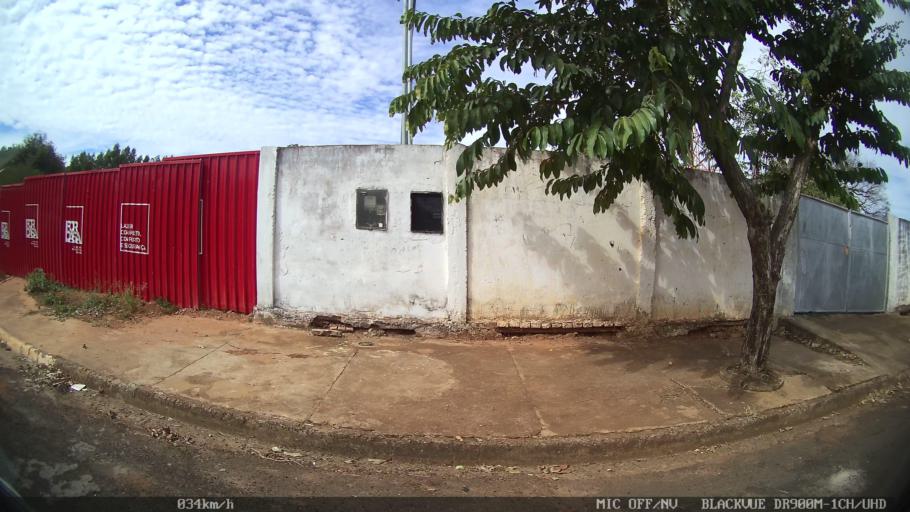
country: BR
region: Sao Paulo
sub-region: Catanduva
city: Catanduva
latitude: -21.1554
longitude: -48.9724
